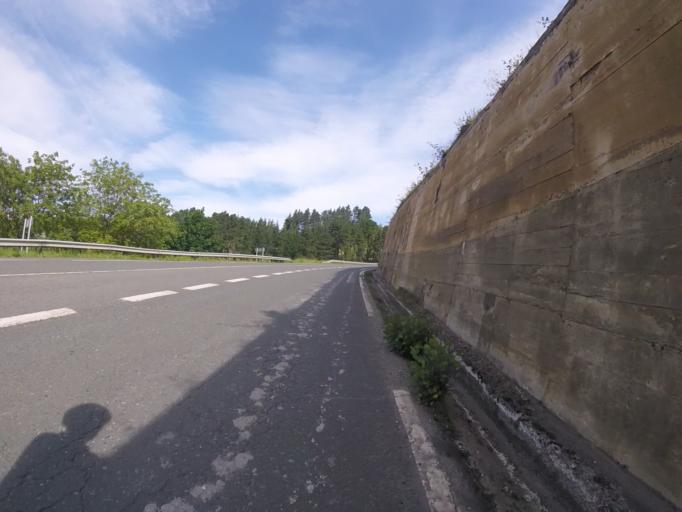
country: ES
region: Basque Country
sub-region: Provincia de Guipuzcoa
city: Zumarraga
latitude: 43.0840
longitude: -2.3040
